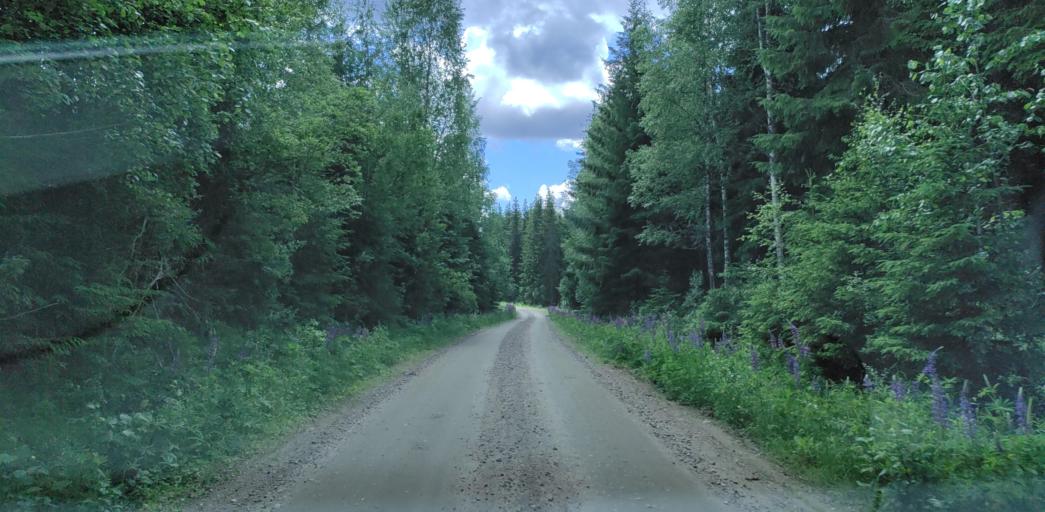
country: SE
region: Vaermland
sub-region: Hagfors Kommun
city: Ekshaerad
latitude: 60.0783
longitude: 13.3139
